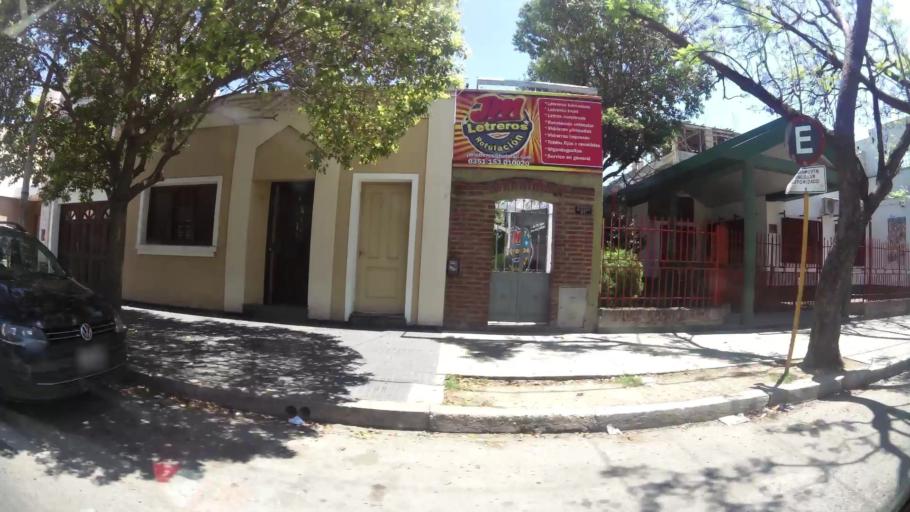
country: AR
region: Cordoba
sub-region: Departamento de Capital
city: Cordoba
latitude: -31.4045
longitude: -64.2189
